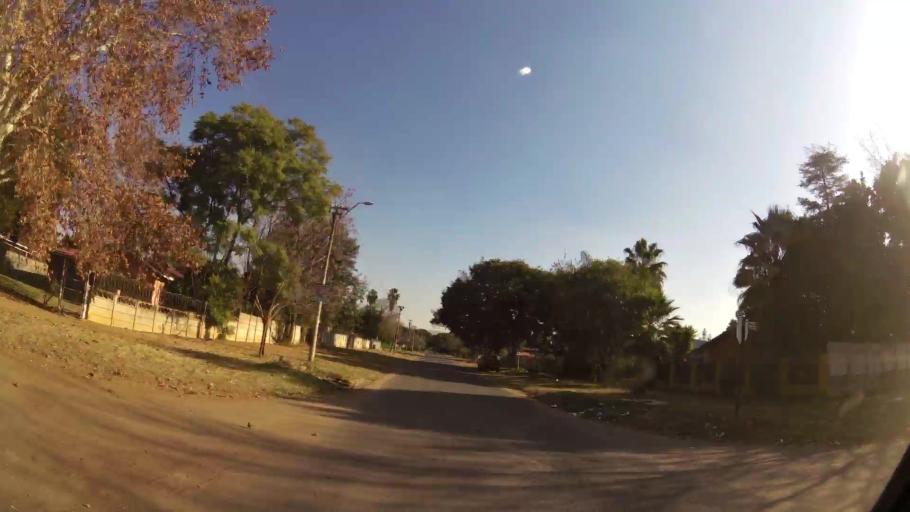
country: ZA
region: North-West
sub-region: Bojanala Platinum District Municipality
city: Rustenburg
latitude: -25.6516
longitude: 27.2528
